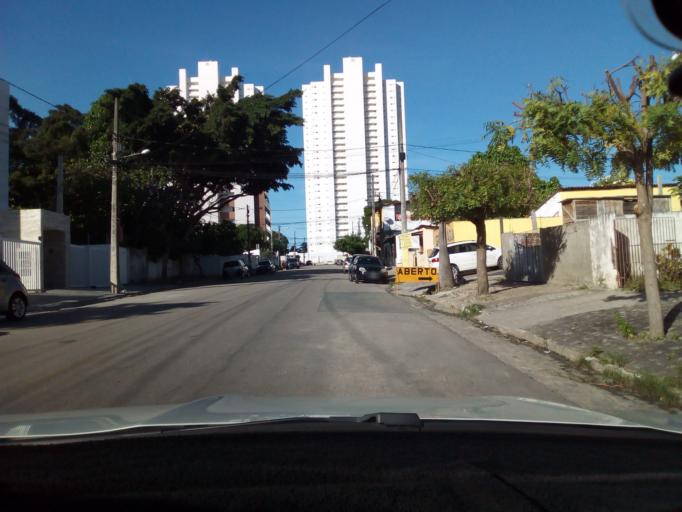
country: BR
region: Paraiba
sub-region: Joao Pessoa
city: Joao Pessoa
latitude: -7.1391
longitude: -34.8295
